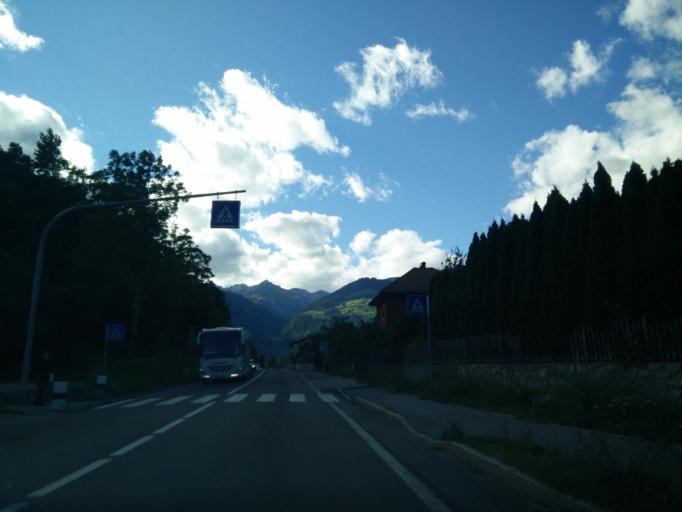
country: IT
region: Trentino-Alto Adige
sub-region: Bolzano
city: Glorenza
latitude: 46.6804
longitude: 10.5636
